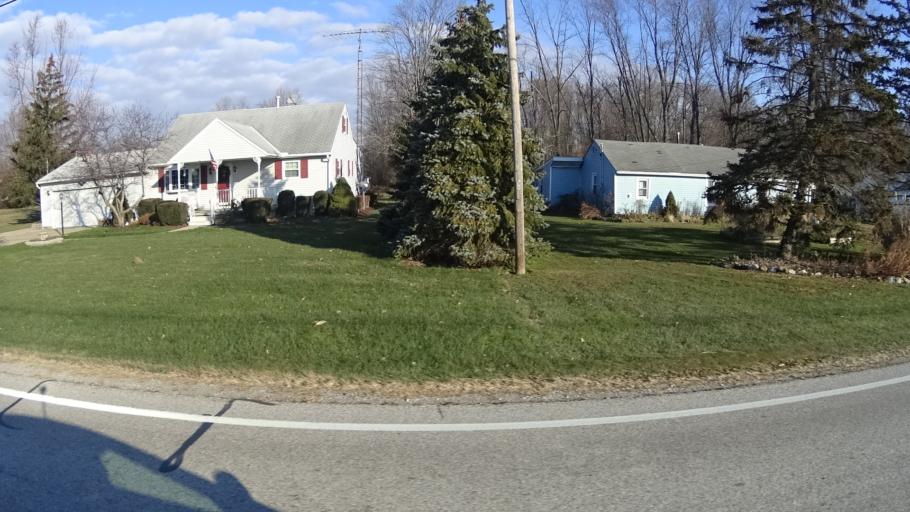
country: US
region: Ohio
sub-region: Lorain County
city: Oberlin
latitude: 41.2810
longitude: -82.1774
